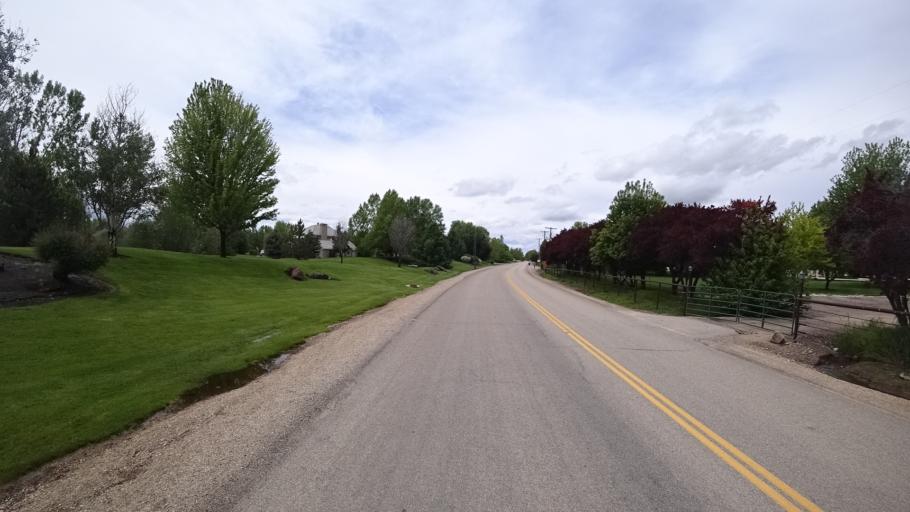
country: US
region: Idaho
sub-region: Ada County
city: Star
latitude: 43.6892
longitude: -116.4391
